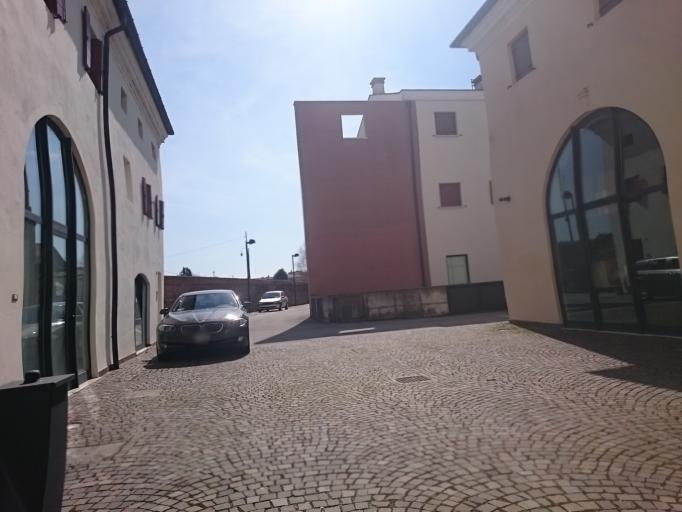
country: IT
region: Veneto
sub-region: Provincia di Padova
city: Limena
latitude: 45.4816
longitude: 11.8439
